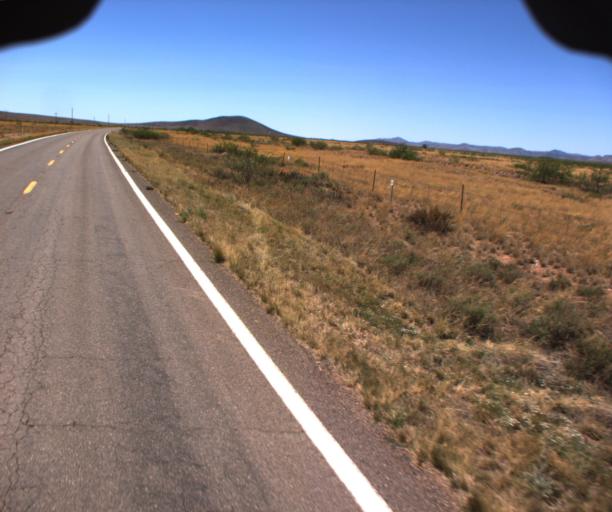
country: US
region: Arizona
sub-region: Cochise County
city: Douglas
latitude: 31.6560
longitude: -109.1569
